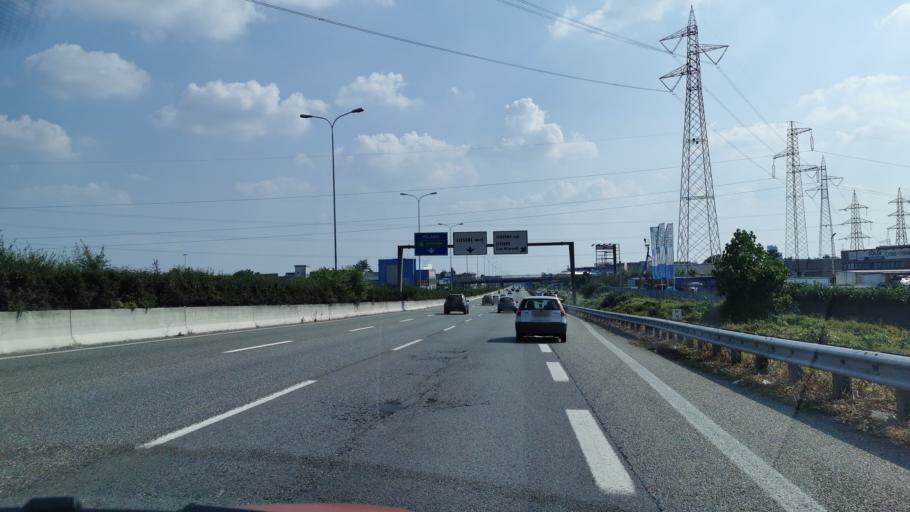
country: IT
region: Lombardy
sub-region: Provincia di Monza e Brianza
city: Santa Margherita
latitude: 45.6399
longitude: 9.2250
